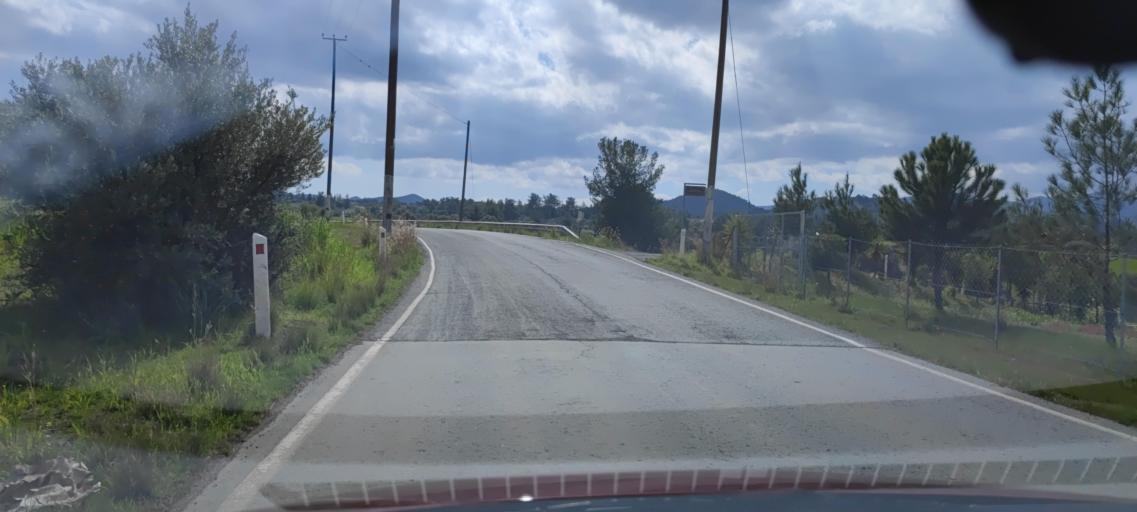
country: CY
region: Lefkosia
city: Lythrodontas
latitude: 34.9872
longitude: 33.2963
